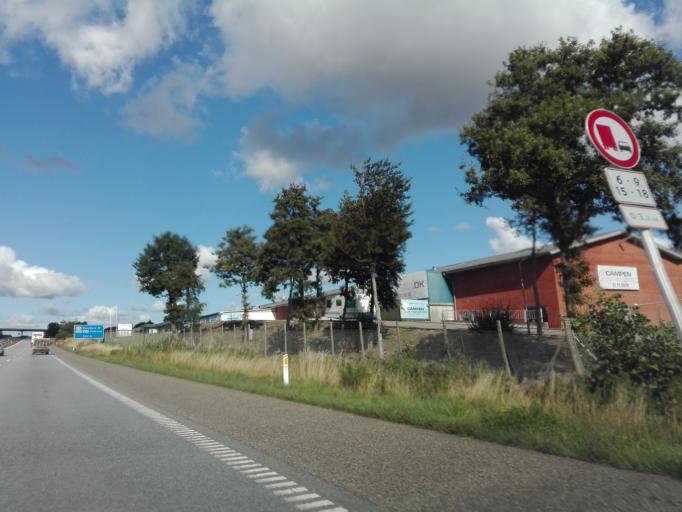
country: DK
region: Central Jutland
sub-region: Randers Kommune
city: Randers
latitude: 56.4806
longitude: 9.9813
